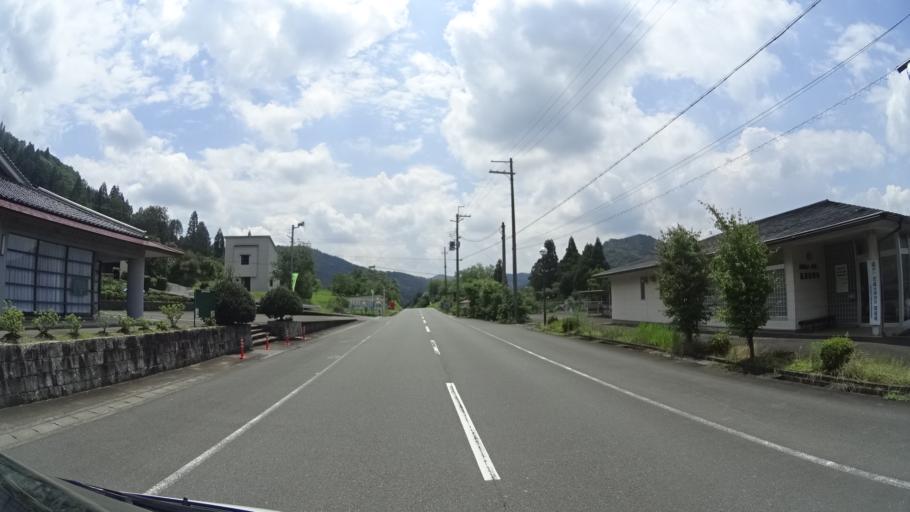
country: JP
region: Kyoto
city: Ayabe
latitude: 35.1998
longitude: 135.2617
